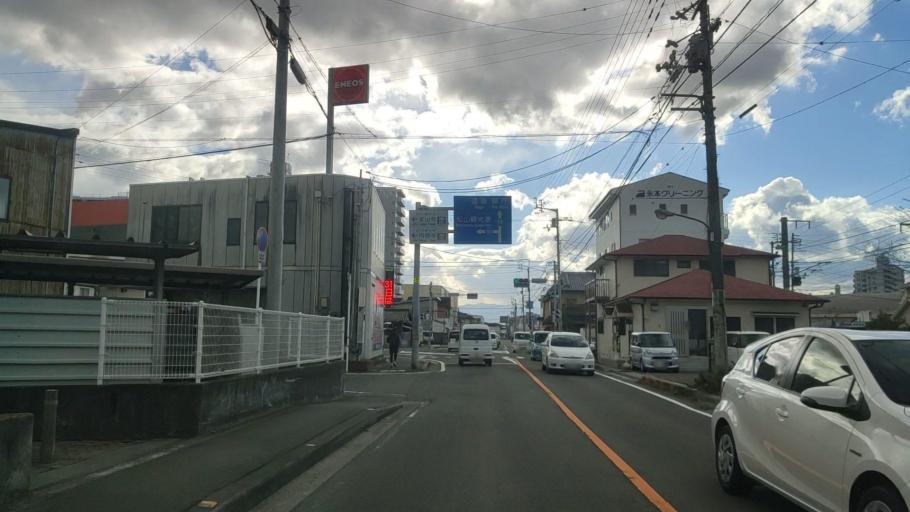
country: JP
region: Ehime
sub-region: Shikoku-chuo Shi
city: Matsuyama
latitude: 33.8682
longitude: 132.7178
